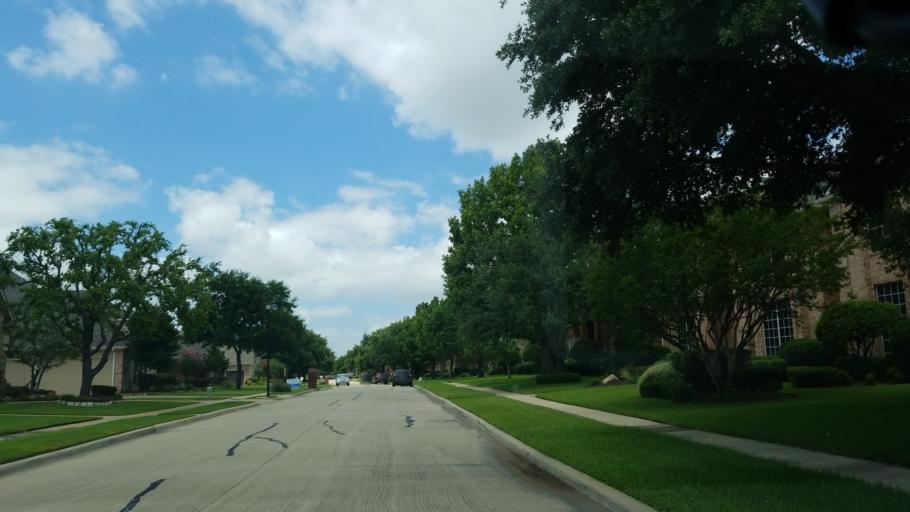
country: US
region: Texas
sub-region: Dallas County
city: Carrollton
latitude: 32.9566
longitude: -96.9495
